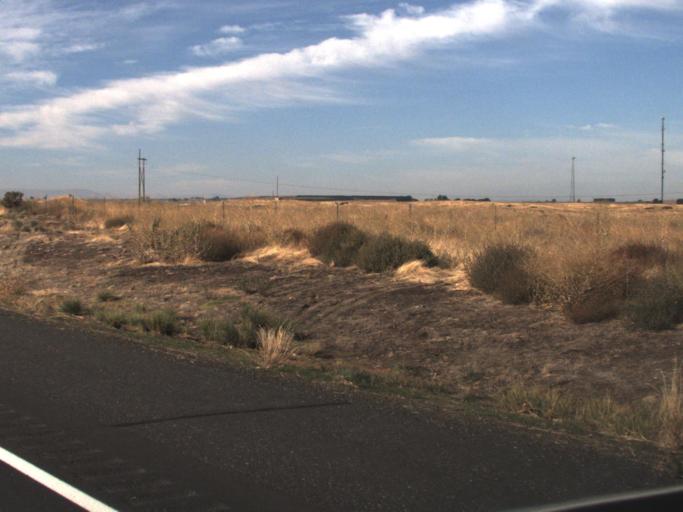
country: US
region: Washington
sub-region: Franklin County
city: Connell
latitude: 46.5759
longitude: -118.9815
